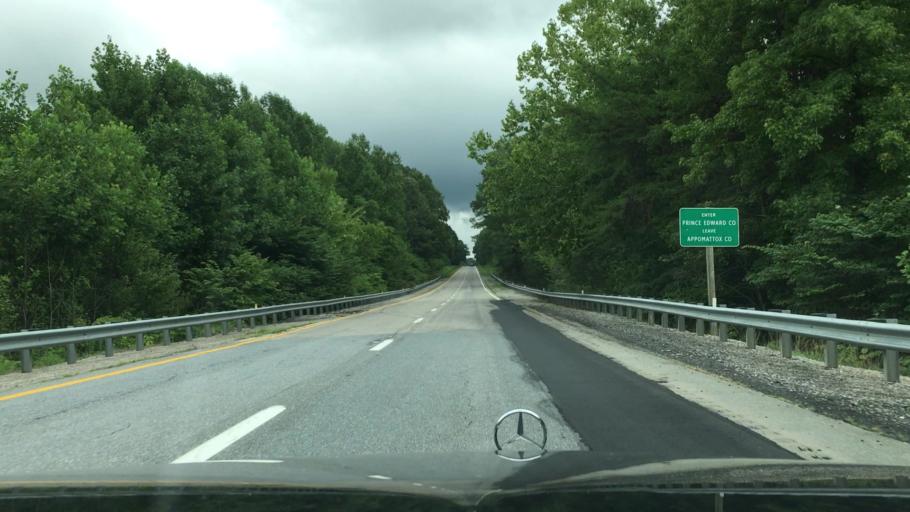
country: US
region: Virginia
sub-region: Appomattox County
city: Appomattox
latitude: 37.2706
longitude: -78.6710
